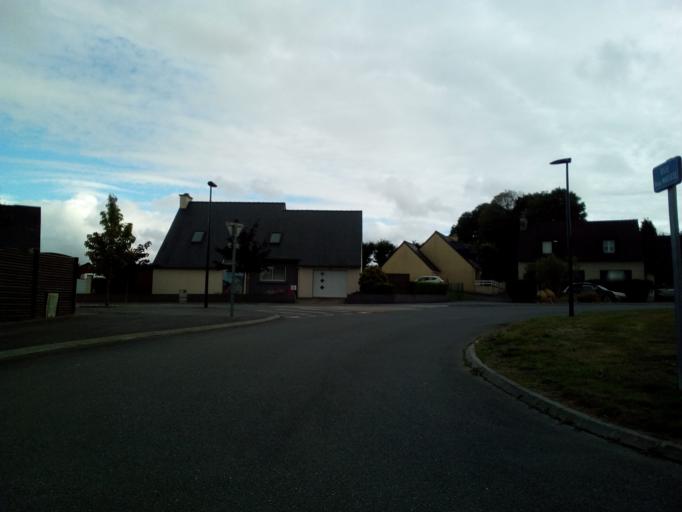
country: FR
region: Brittany
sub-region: Departement du Finistere
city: Landivisiau
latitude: 48.5077
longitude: -4.0584
